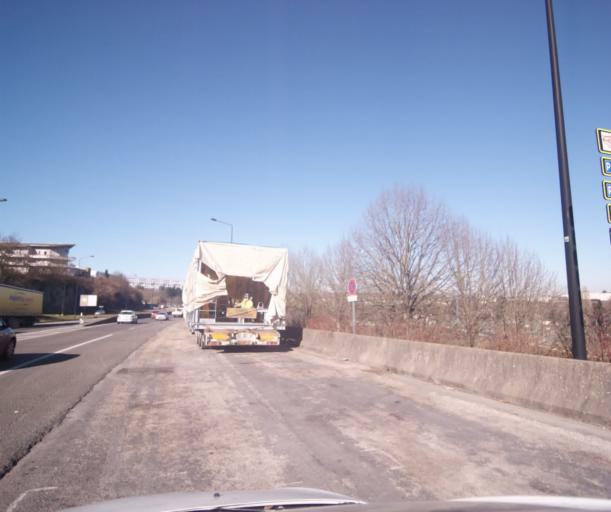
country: FR
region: Franche-Comte
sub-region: Departement du Doubs
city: Beure
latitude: 47.2183
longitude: 5.9835
